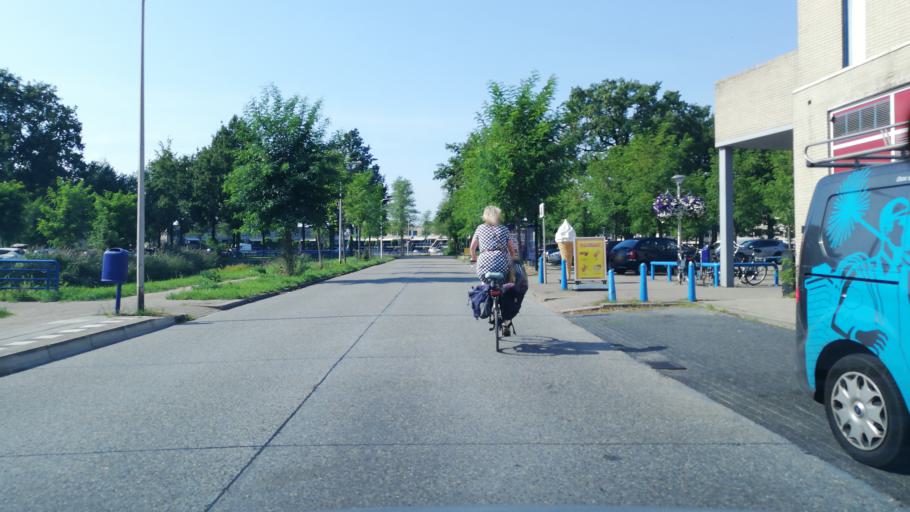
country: NL
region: Overijssel
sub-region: Gemeente Zwolle
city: Zwolle
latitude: 52.4968
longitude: 6.0939
